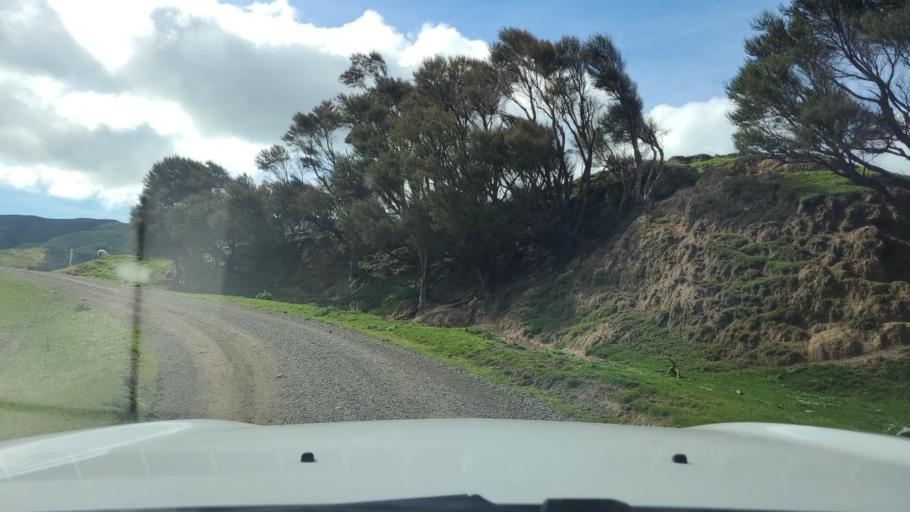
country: NZ
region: Wellington
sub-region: South Wairarapa District
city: Waipawa
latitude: -41.3797
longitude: 175.7231
